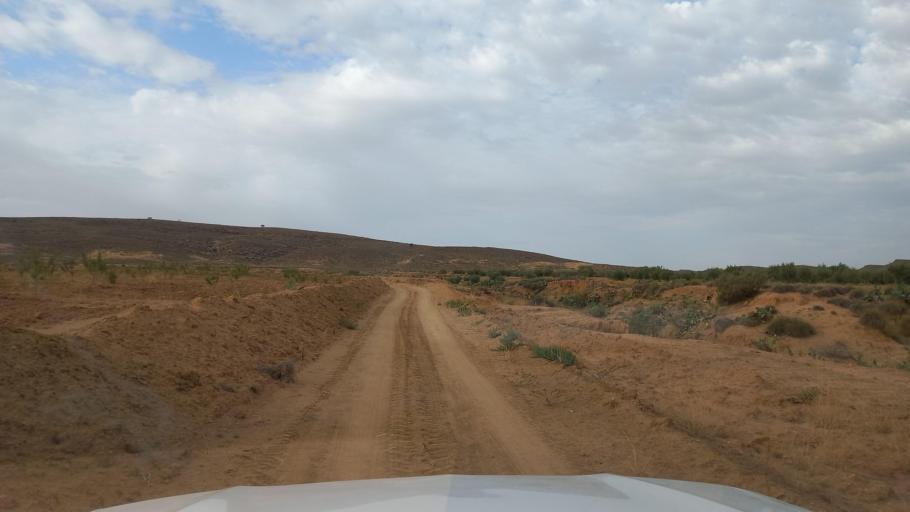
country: TN
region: Al Qasrayn
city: Kasserine
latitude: 35.1866
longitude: 9.0477
